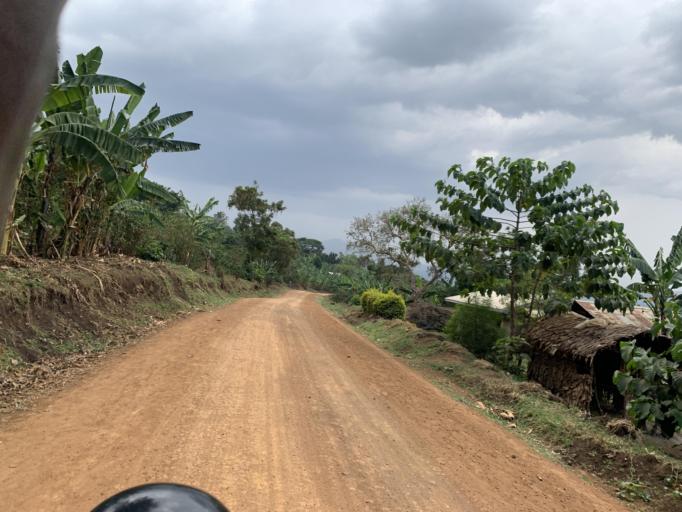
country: UG
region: Eastern Region
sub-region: Sironko District
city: Sironko
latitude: 1.2590
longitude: 34.2922
